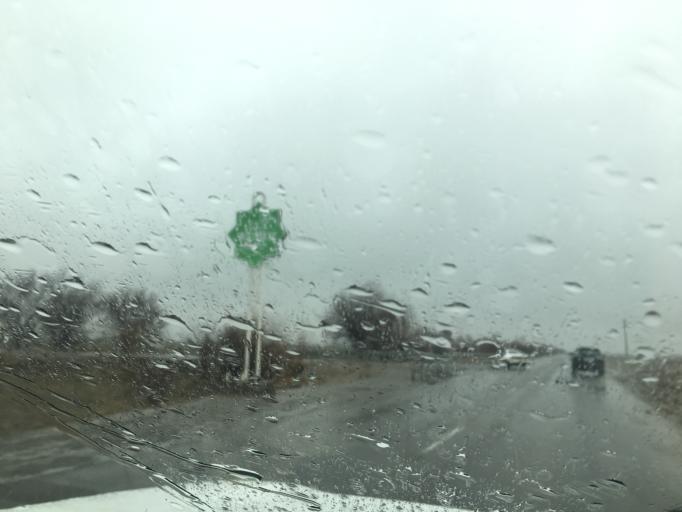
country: TM
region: Mary
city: Yoloeten
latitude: 37.3587
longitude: 62.2389
